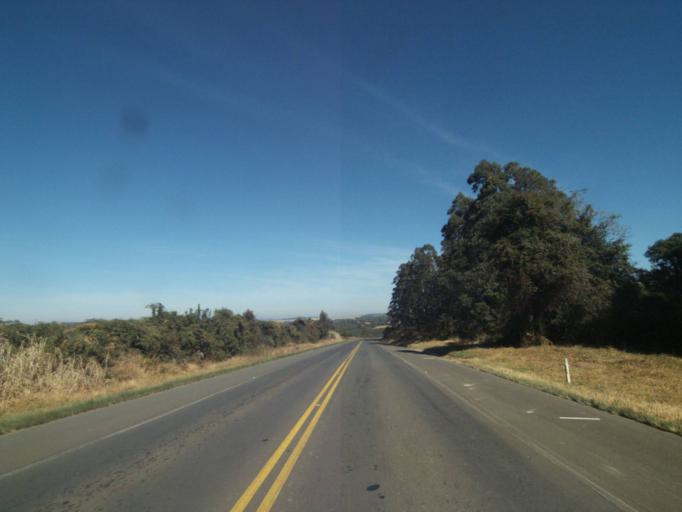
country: BR
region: Parana
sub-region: Tibagi
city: Tibagi
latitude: -24.8057
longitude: -50.4724
